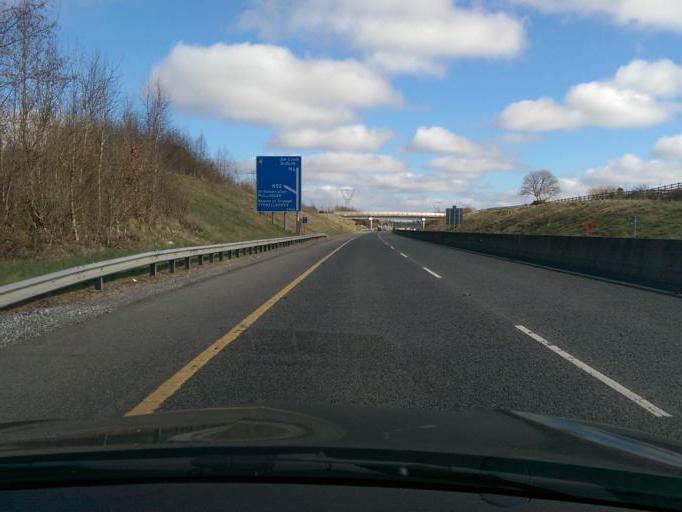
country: IE
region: Leinster
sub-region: An Iarmhi
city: Rochfortbridge
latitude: 53.3817
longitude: -7.3763
